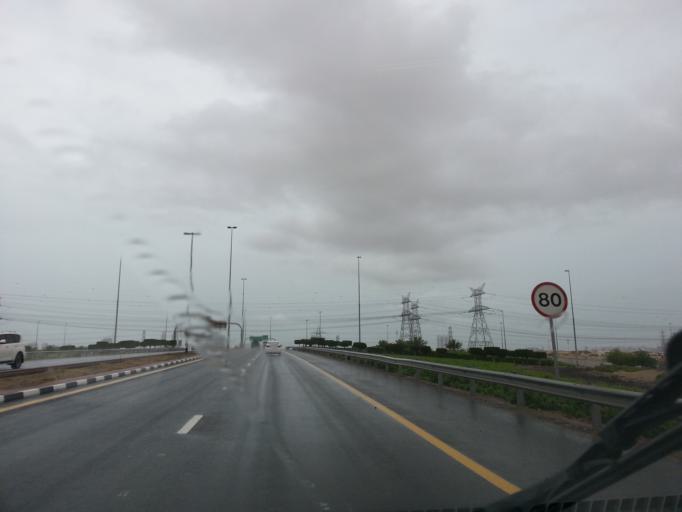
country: AE
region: Dubai
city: Dubai
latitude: 25.0750
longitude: 55.2128
